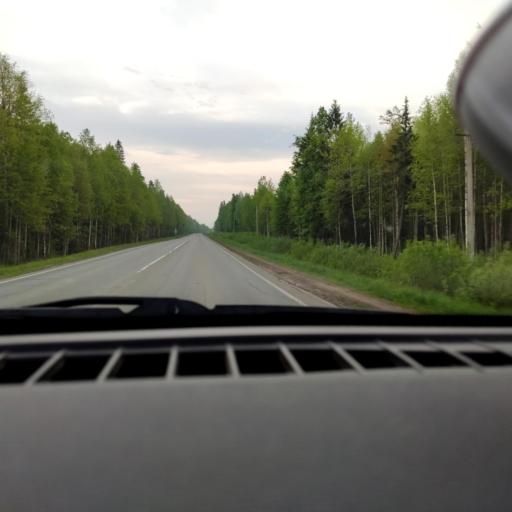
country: RU
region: Perm
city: Perm
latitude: 58.2129
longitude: 56.1809
